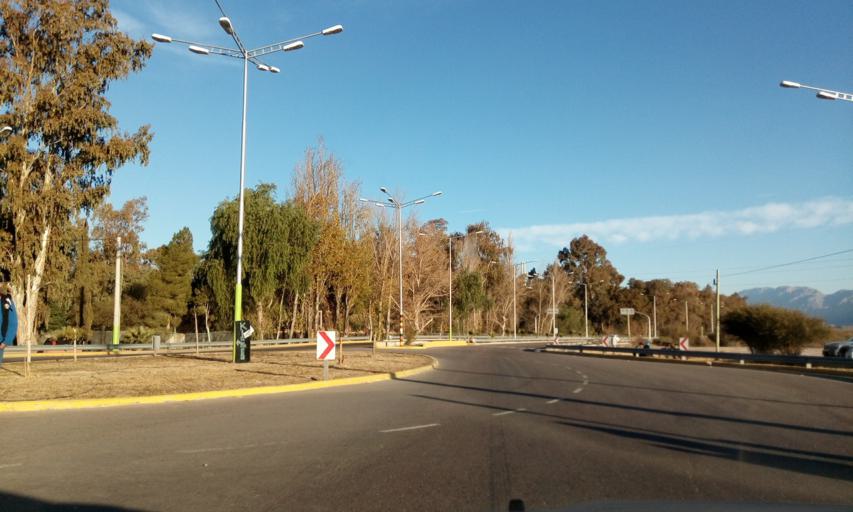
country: AR
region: San Juan
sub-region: Departamento de Rivadavia
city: Rivadavia
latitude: -31.5054
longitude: -68.6449
